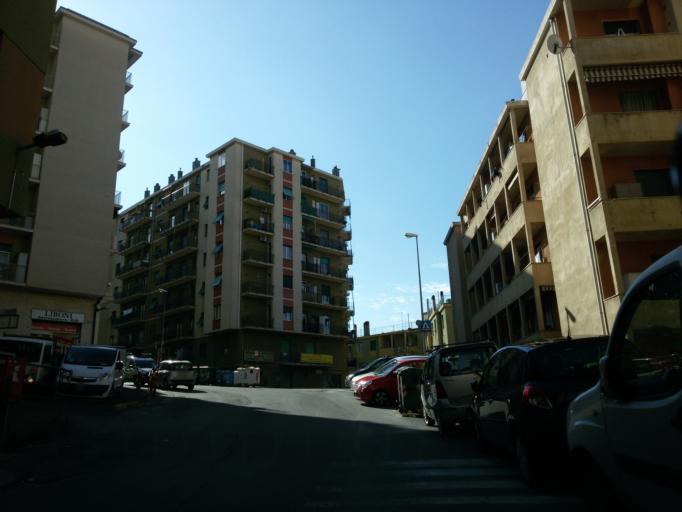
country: IT
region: Liguria
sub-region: Provincia di Genova
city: Genoa
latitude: 44.4111
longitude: 8.9603
